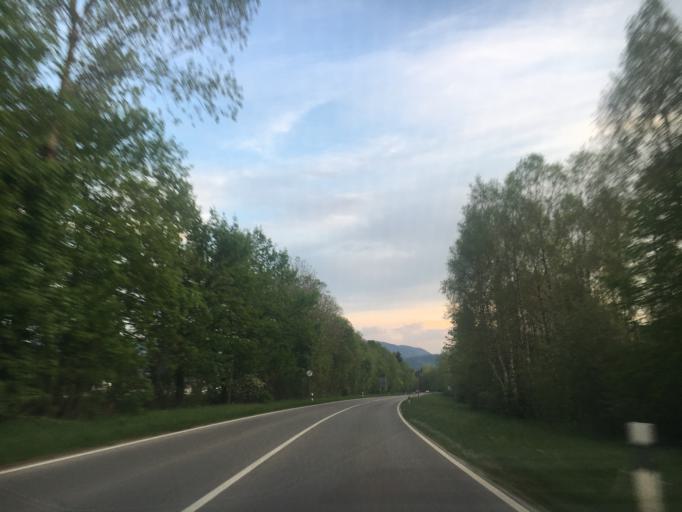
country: DE
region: Bavaria
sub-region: Upper Bavaria
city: Lenggries
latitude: 47.6804
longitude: 11.5724
